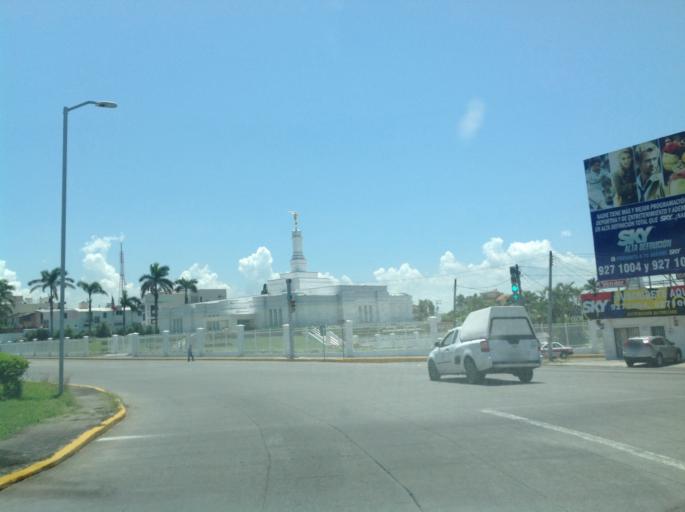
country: MX
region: Veracruz
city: Boca del Rio
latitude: 19.1352
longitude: -96.1054
